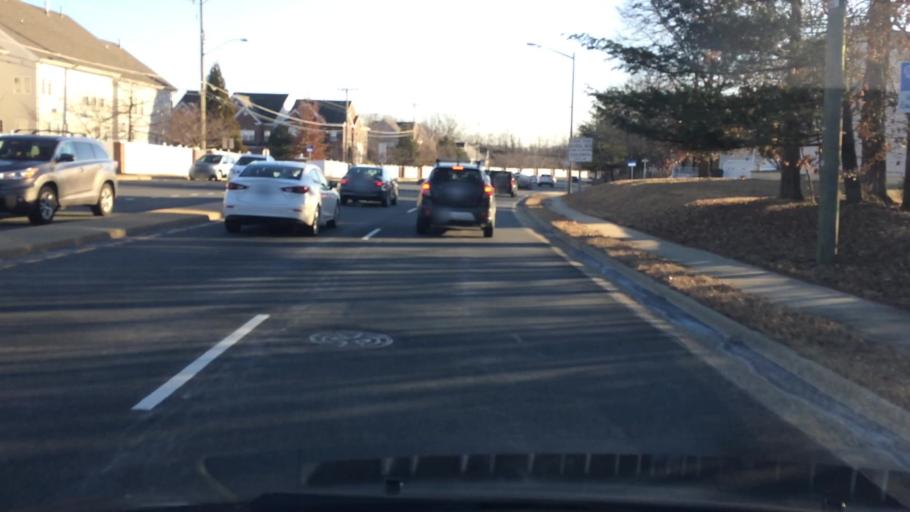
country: US
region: Virginia
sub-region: City of Fairfax
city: Fairfax
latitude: 38.8500
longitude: -77.3380
